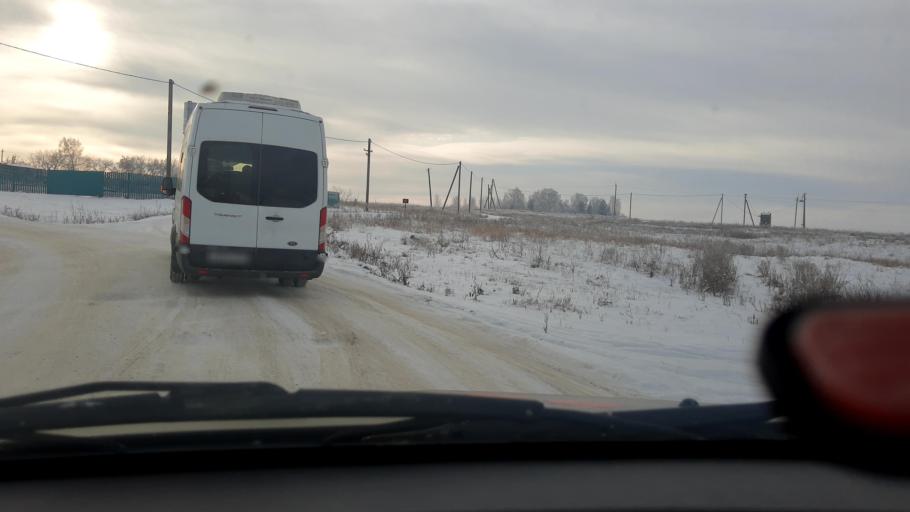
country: RU
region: Bashkortostan
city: Tolbazy
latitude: 54.3559
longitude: 55.8437
